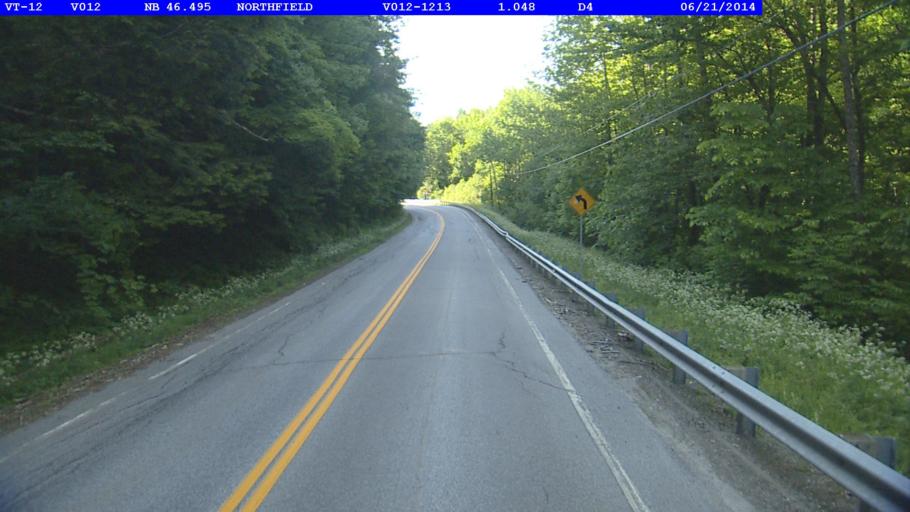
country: US
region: Vermont
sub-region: Washington County
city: Northfield
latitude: 44.1071
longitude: -72.6453
